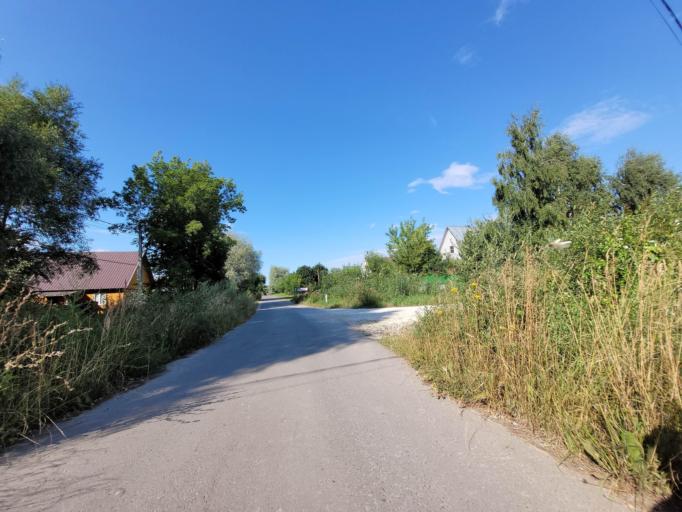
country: RU
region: Moskovskaya
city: Lopatinskiy
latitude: 55.3911
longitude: 38.7147
